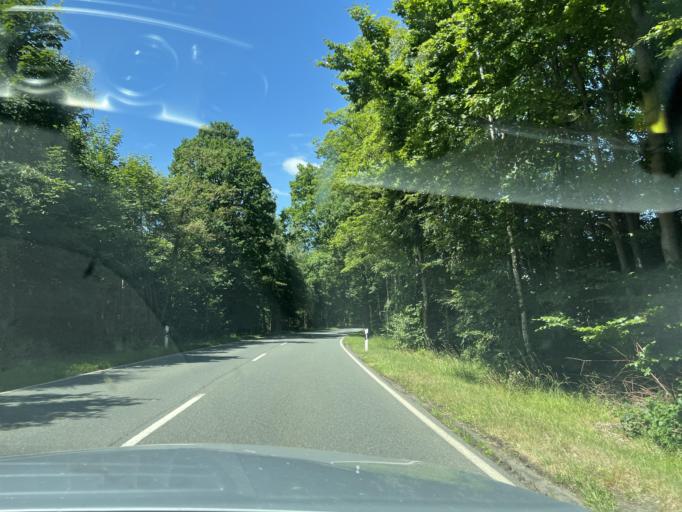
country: DE
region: North Rhine-Westphalia
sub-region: Regierungsbezirk Arnsberg
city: Wenden
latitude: 50.9620
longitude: 7.9239
